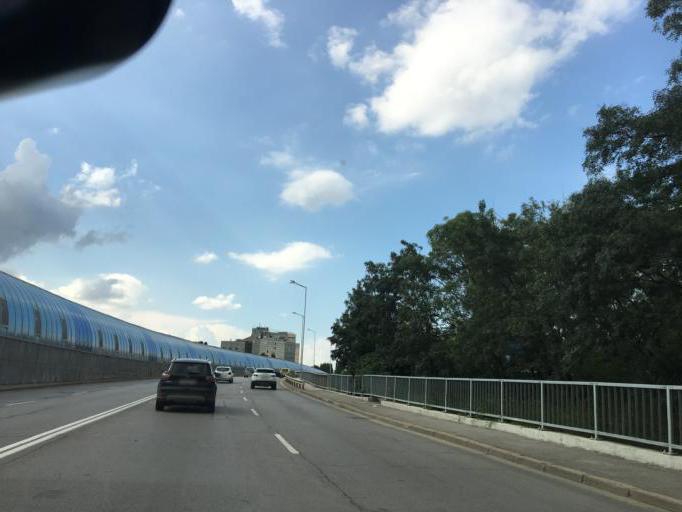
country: BG
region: Sofia-Capital
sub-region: Stolichna Obshtina
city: Sofia
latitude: 42.6663
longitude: 23.3541
